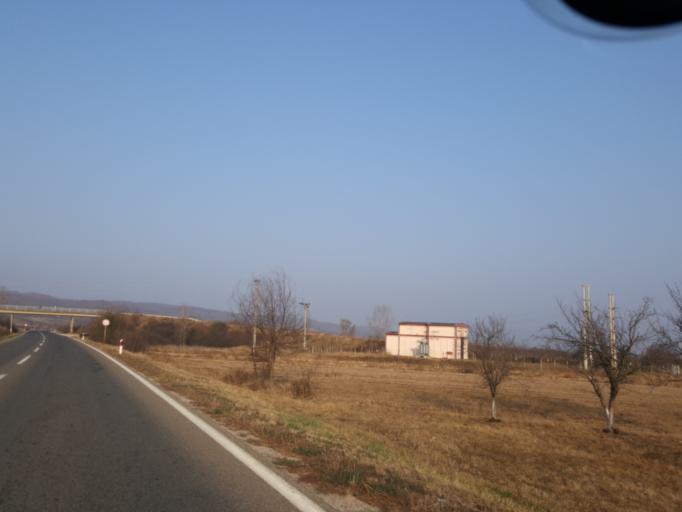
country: RS
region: Central Serbia
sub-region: Jablanicki Okrug
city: Leskovac
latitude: 42.9379
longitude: 22.0043
